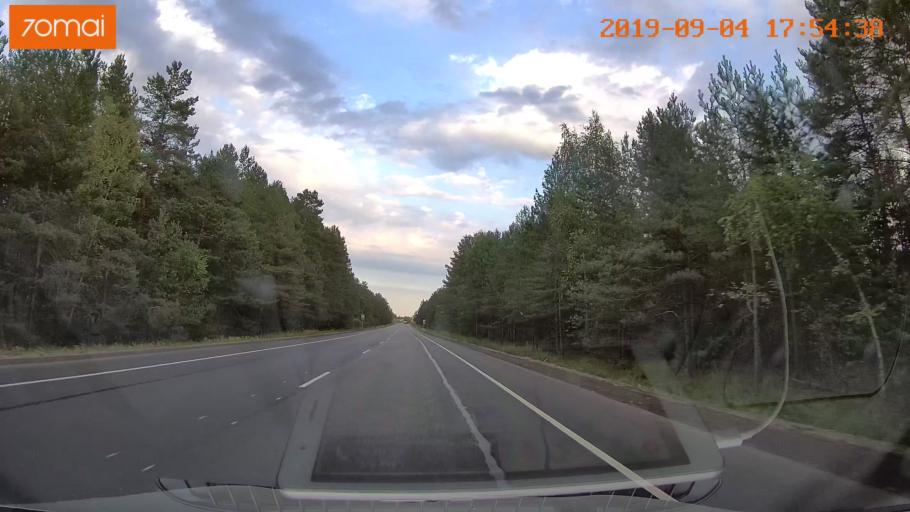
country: RU
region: Moskovskaya
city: Imeni Tsyurupy
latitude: 55.5094
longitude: 38.7499
